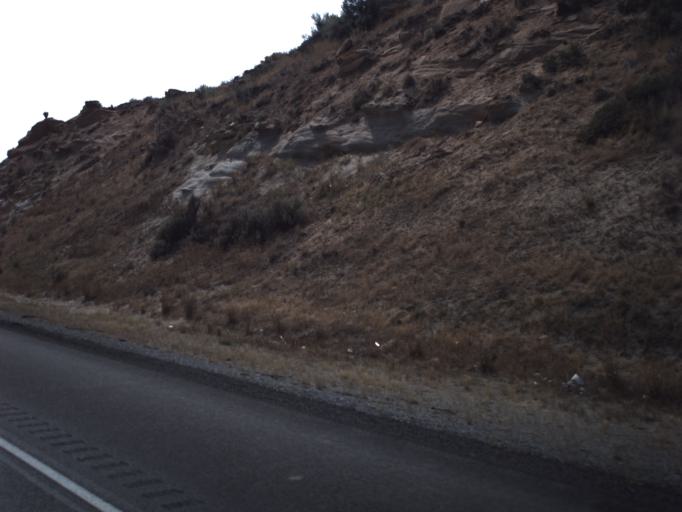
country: US
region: Wyoming
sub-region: Uinta County
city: Evanston
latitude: 41.1668
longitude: -111.1371
